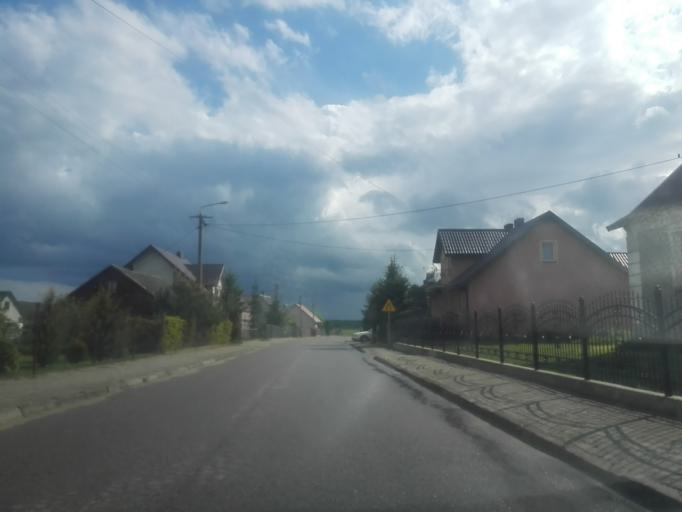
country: PL
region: Podlasie
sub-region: Powiat lomzynski
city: Wizna
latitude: 53.2249
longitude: 22.4193
